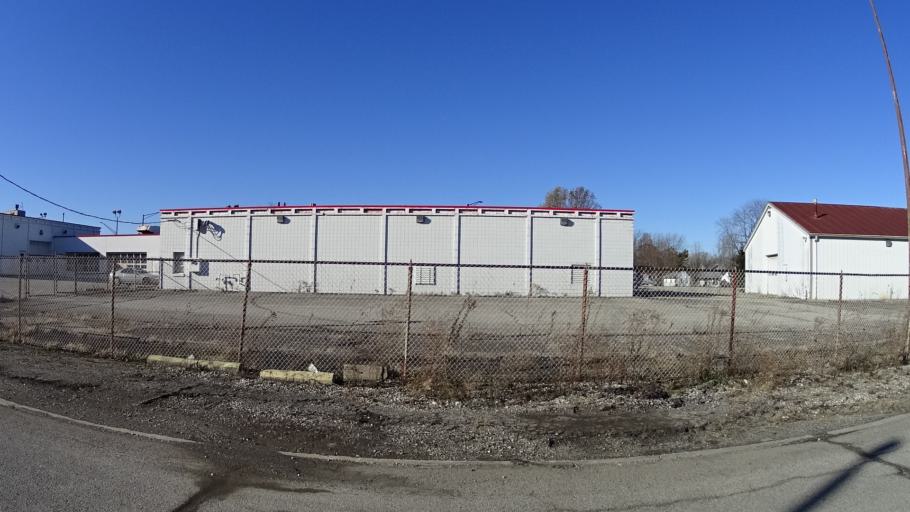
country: US
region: Ohio
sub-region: Lorain County
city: Elyria
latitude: 41.3790
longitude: -82.0752
